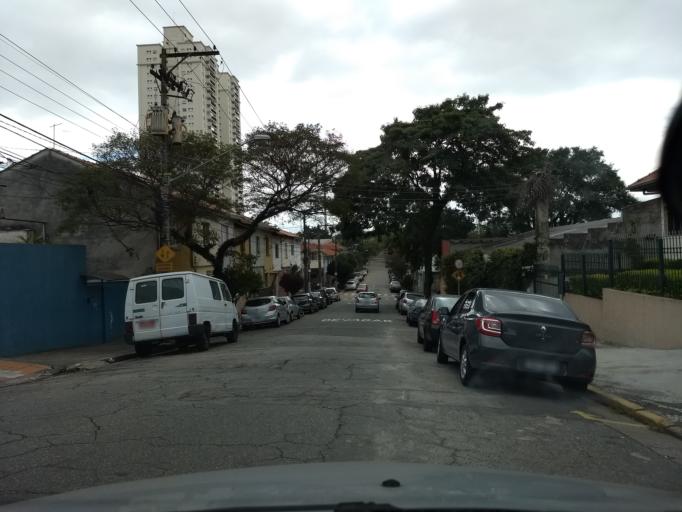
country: BR
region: Sao Paulo
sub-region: Sao Paulo
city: Sao Paulo
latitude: -23.5967
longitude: -46.6110
